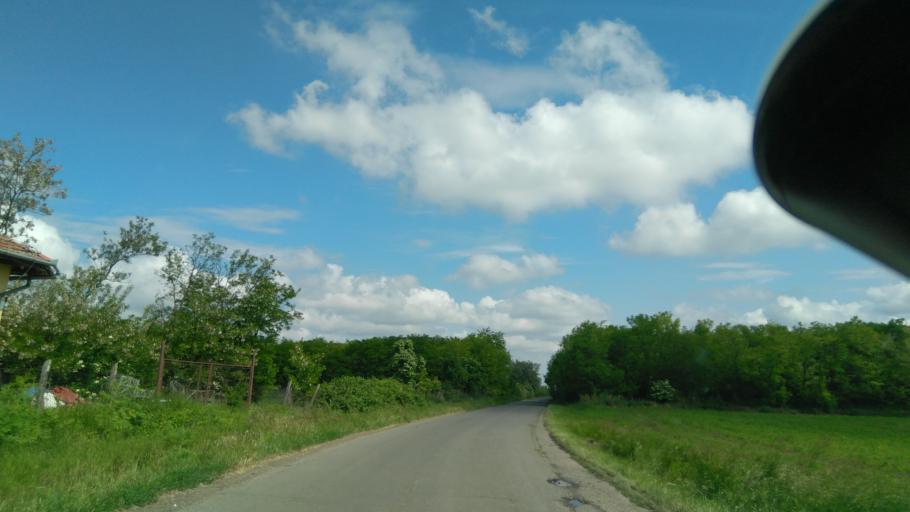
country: HU
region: Bekes
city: Bekes
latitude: 46.8219
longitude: 21.1376
